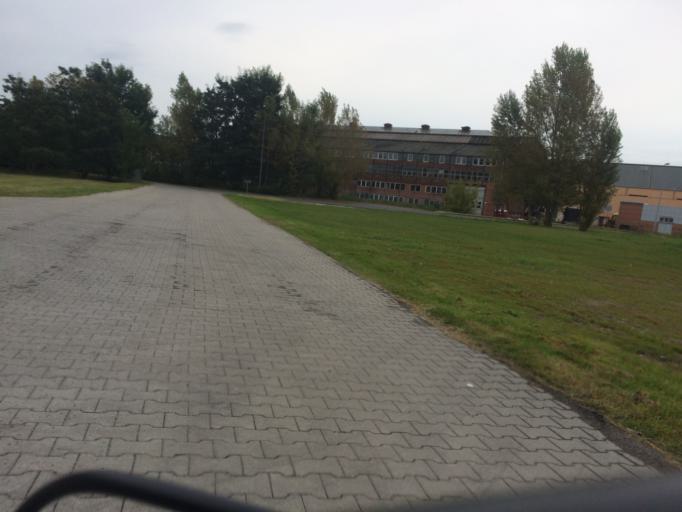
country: DE
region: Berlin
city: Markisches Viertel
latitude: 52.5879
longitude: 13.3518
